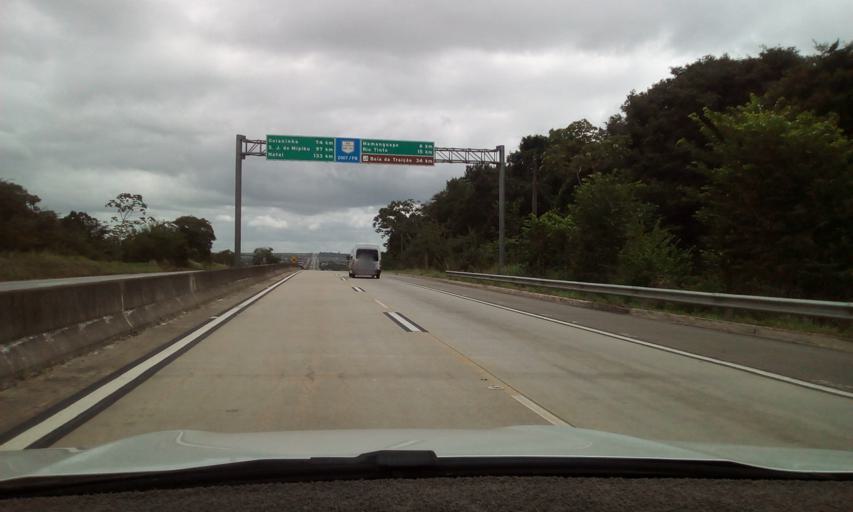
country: BR
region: Paraiba
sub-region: Mamanguape
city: Mamanguape
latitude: -6.8695
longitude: -35.1328
